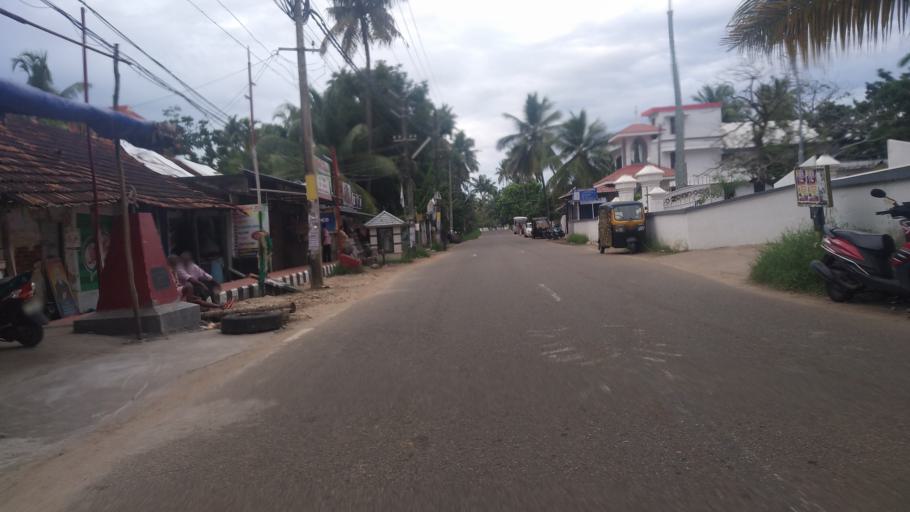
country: IN
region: Kerala
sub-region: Ernakulam
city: Cochin
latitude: 9.8934
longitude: 76.2591
